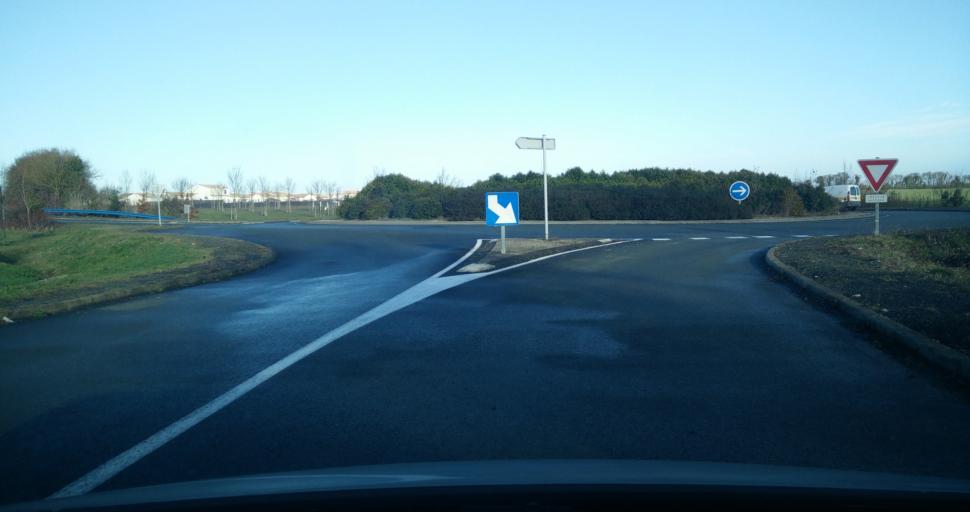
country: FR
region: Poitou-Charentes
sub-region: Departement de la Charente-Maritime
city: Saint-Xandre
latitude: 46.2042
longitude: -1.0876
